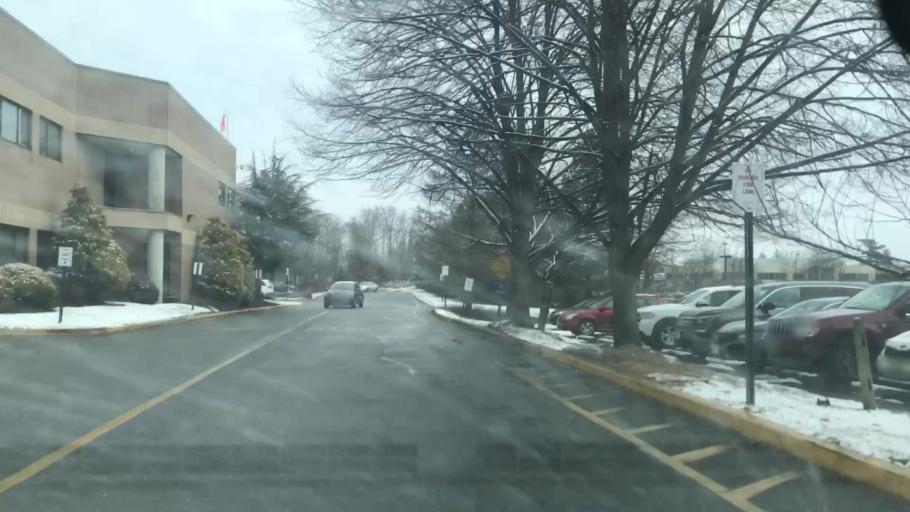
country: US
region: New Jersey
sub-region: Ocean County
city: Lakewood
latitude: 40.0744
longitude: -74.2194
